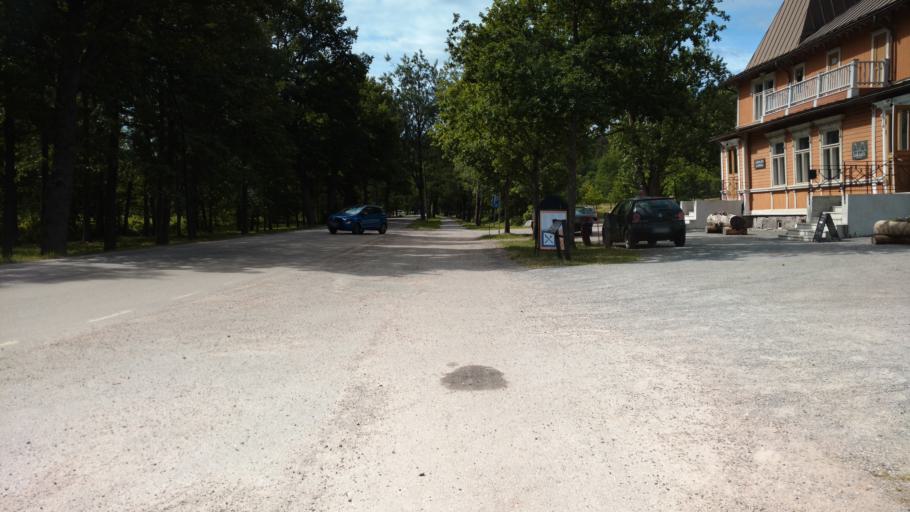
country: FI
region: Uusimaa
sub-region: Raaseporin
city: Pohja
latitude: 60.1271
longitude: 23.5384
